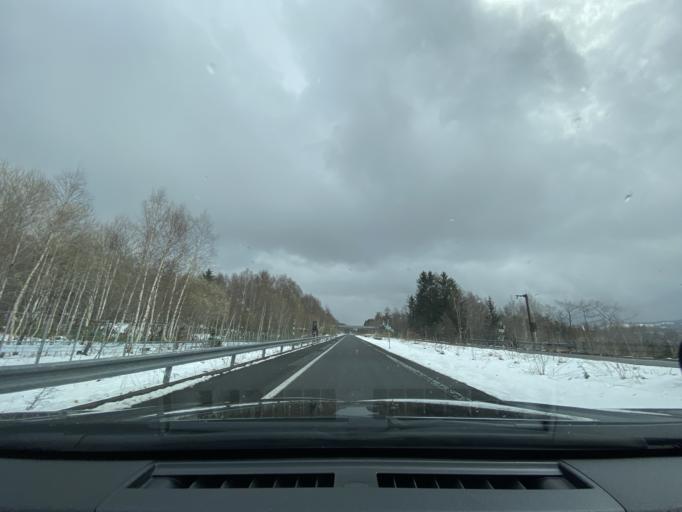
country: JP
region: Hokkaido
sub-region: Asahikawa-shi
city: Asahikawa
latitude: 43.9780
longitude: 142.4600
